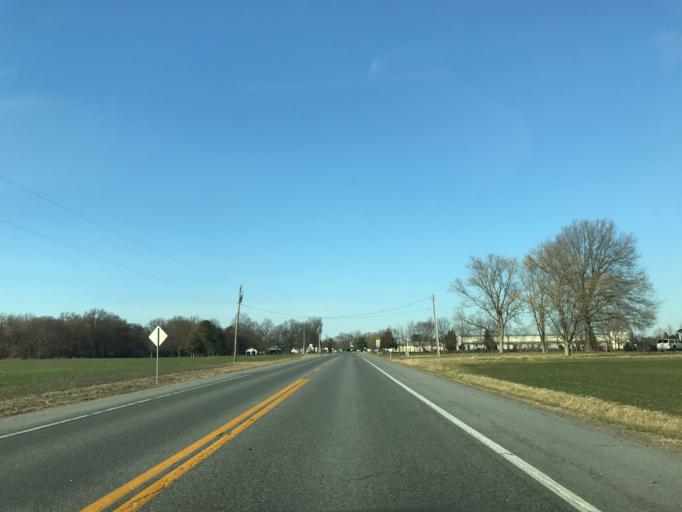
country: US
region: Maryland
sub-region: Caroline County
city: Greensboro
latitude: 39.1373
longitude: -75.8640
